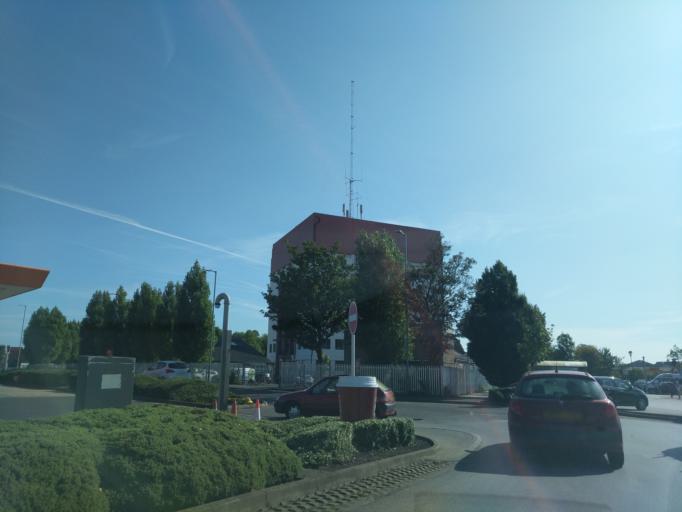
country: GB
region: England
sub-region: Lincolnshire
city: Spalding
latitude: 52.7895
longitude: -0.1560
